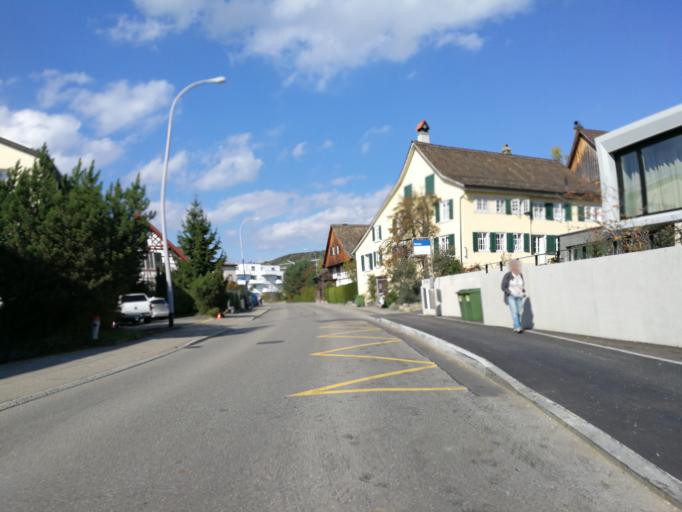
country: CH
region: Zurich
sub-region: Bezirk Meilen
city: Maennedorf / Dorfkern
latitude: 47.2622
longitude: 8.6874
